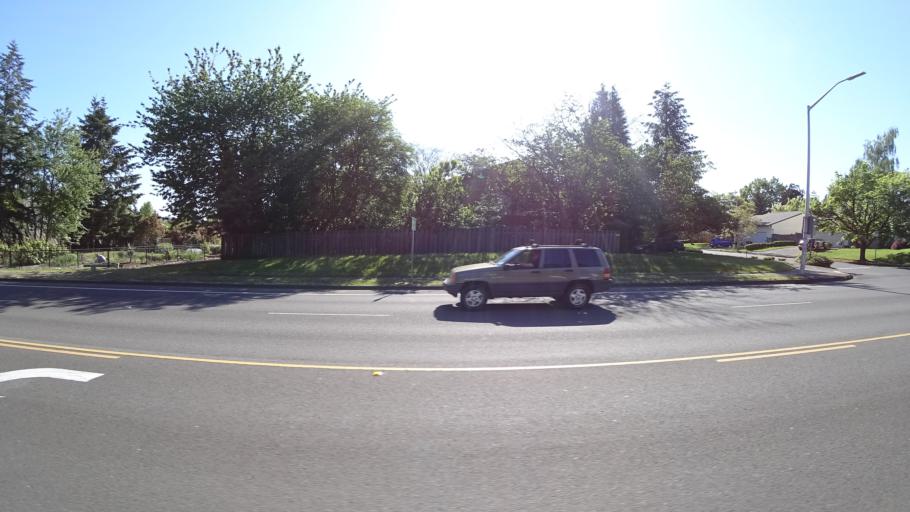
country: US
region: Oregon
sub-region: Washington County
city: Beaverton
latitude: 45.4680
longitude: -122.8038
